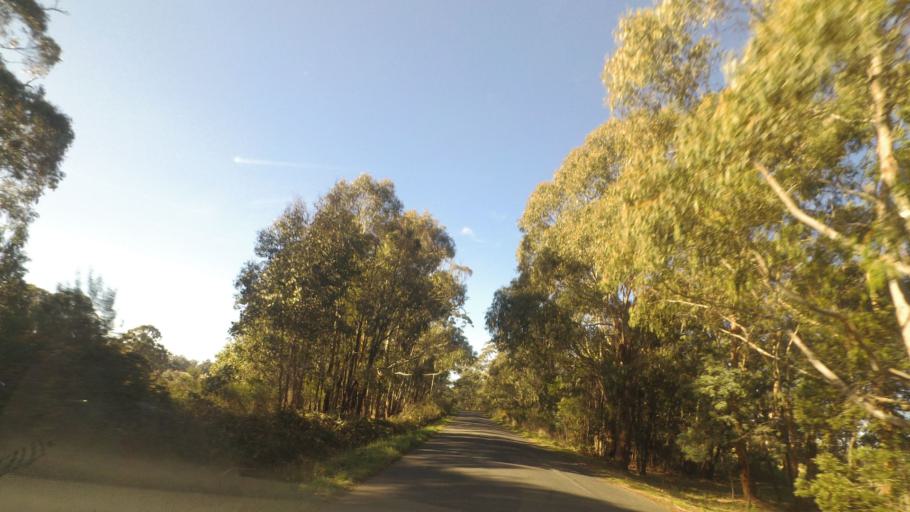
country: AU
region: Victoria
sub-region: Mount Alexander
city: Castlemaine
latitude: -37.3217
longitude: 144.3229
